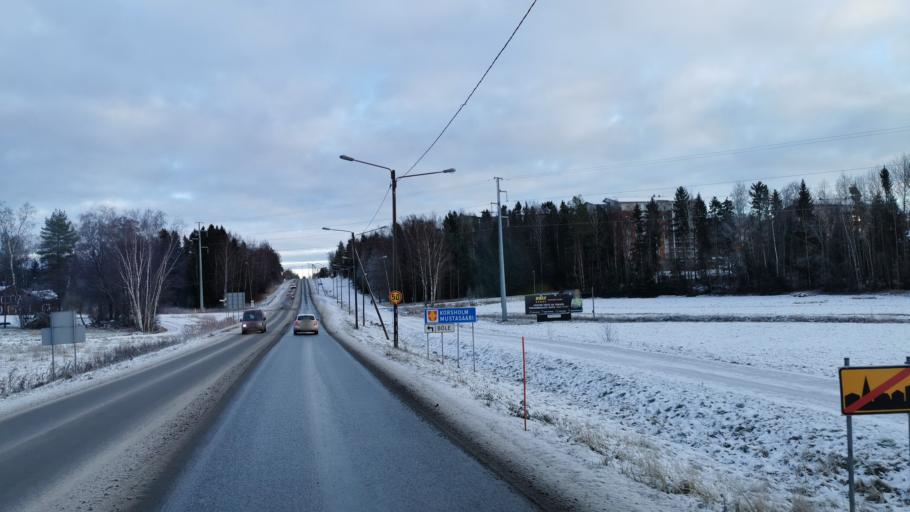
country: FI
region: Ostrobothnia
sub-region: Vaasa
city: Korsholm
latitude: 63.1100
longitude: 21.6660
